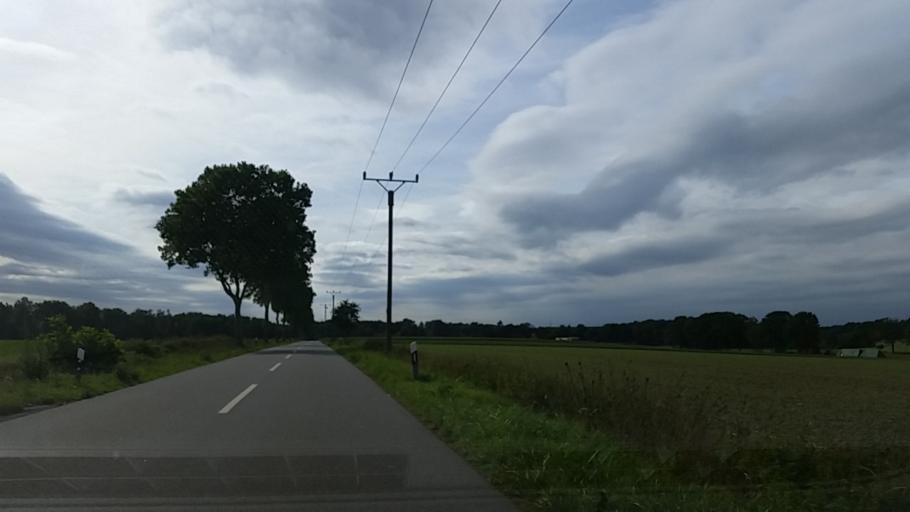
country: DE
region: Lower Saxony
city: Schwienau
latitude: 53.0009
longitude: 10.4260
